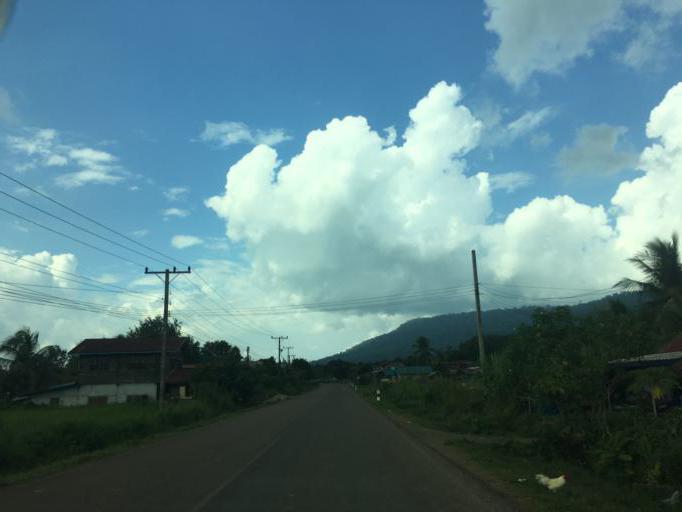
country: TH
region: Nong Khai
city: Sangkhom
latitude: 18.1587
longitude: 102.2623
